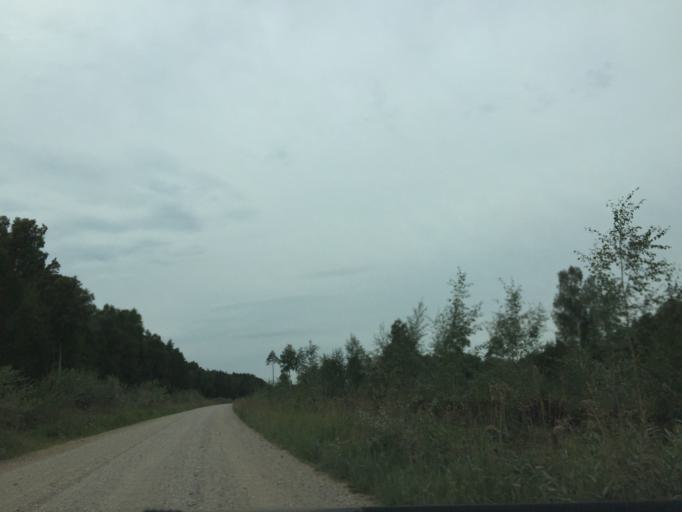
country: LV
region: Jaunpils
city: Jaunpils
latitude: 56.7335
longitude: 23.0955
